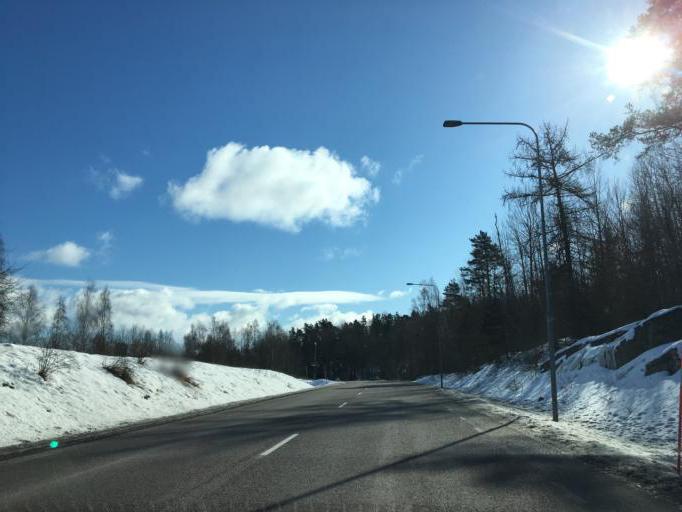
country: SE
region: Vaestmanland
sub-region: Vasteras
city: Vasteras
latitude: 59.6254
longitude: 16.4862
